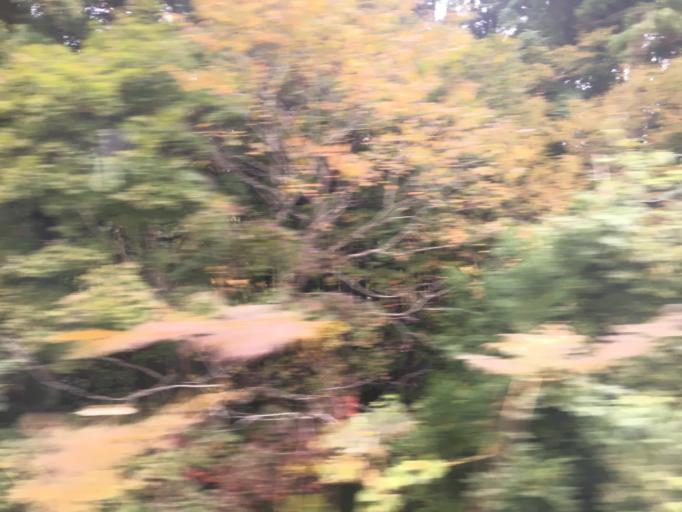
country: JP
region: Niigata
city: Murakami
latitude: 38.0620
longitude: 139.6719
